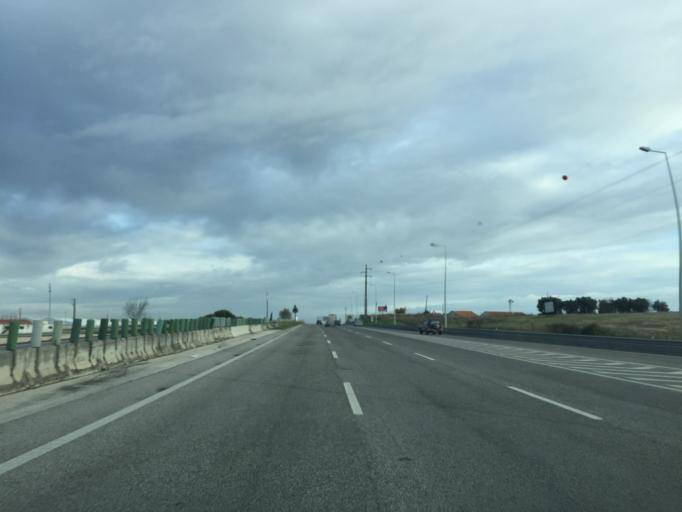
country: PT
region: Lisbon
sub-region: Alenquer
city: Carregado
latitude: 39.0276
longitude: -8.9617
